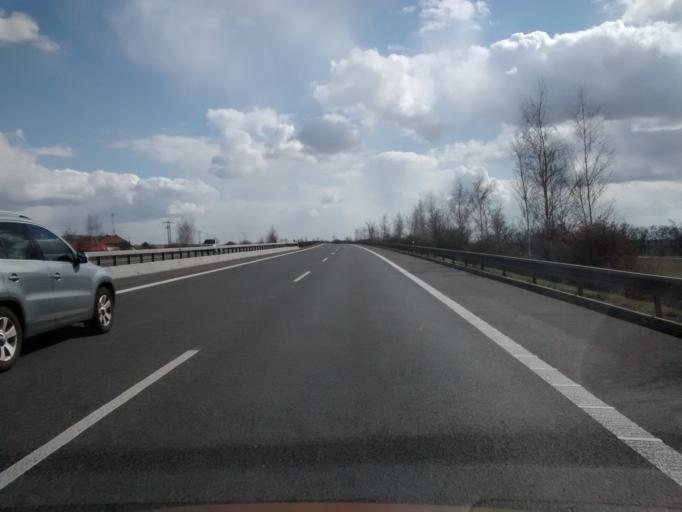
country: CZ
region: Central Bohemia
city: Velvary
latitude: 50.3401
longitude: 14.2814
